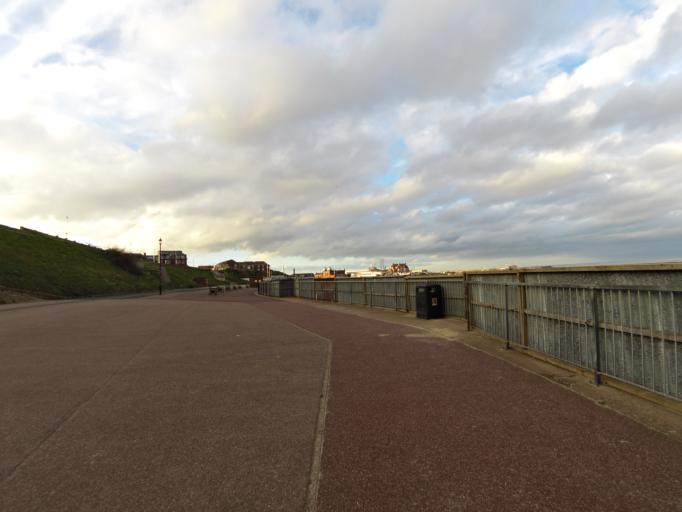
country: GB
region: England
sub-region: Norfolk
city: Gorleston-on-Sea
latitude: 52.5678
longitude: 1.7312
